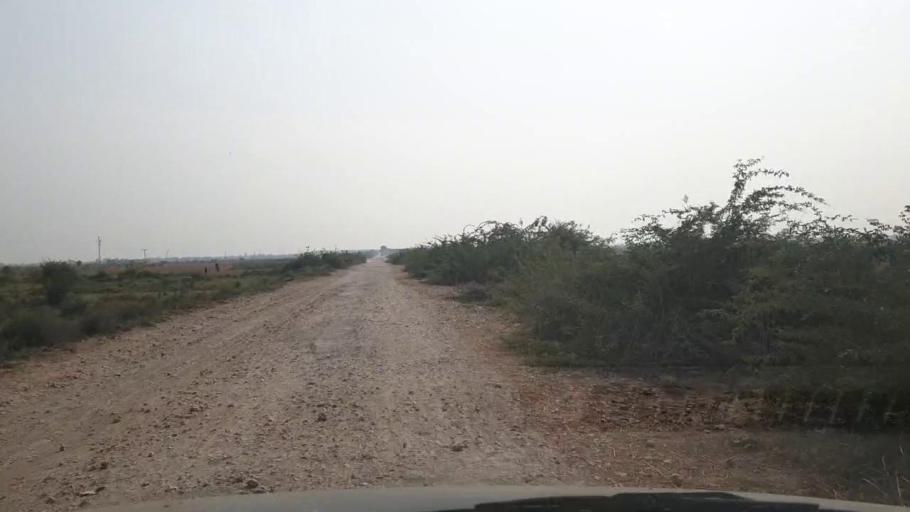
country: PK
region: Sindh
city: Tando Muhammad Khan
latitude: 25.0498
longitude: 68.3887
